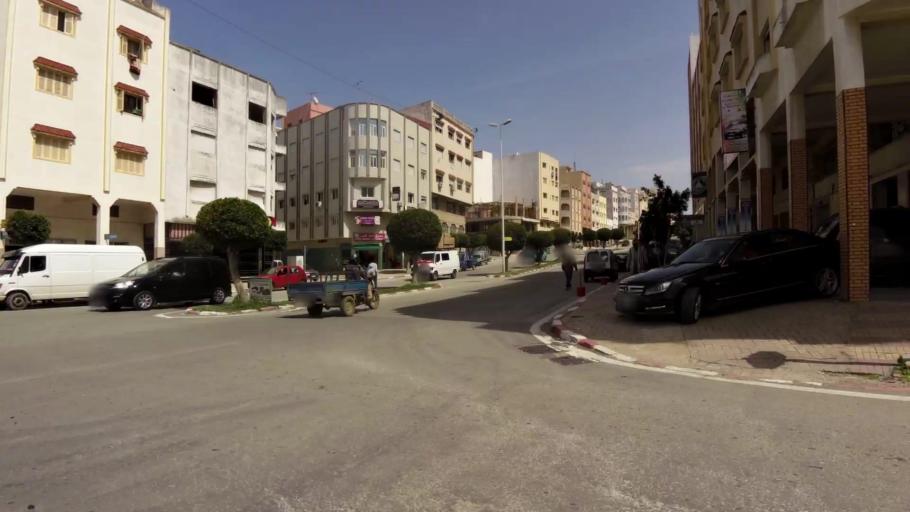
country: MA
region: Tanger-Tetouan
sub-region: Tanger-Assilah
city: Tangier
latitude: 35.7514
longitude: -5.8328
